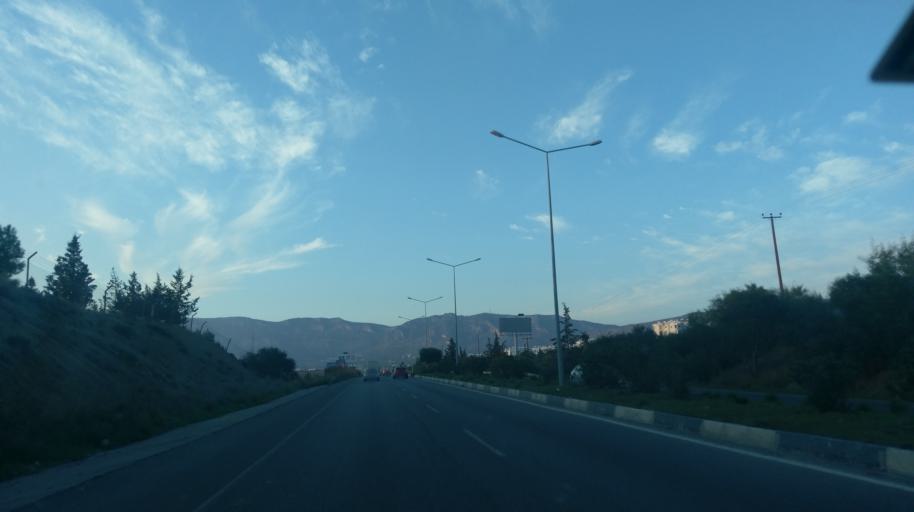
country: CY
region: Keryneia
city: Kyrenia
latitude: 35.2512
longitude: 33.3033
